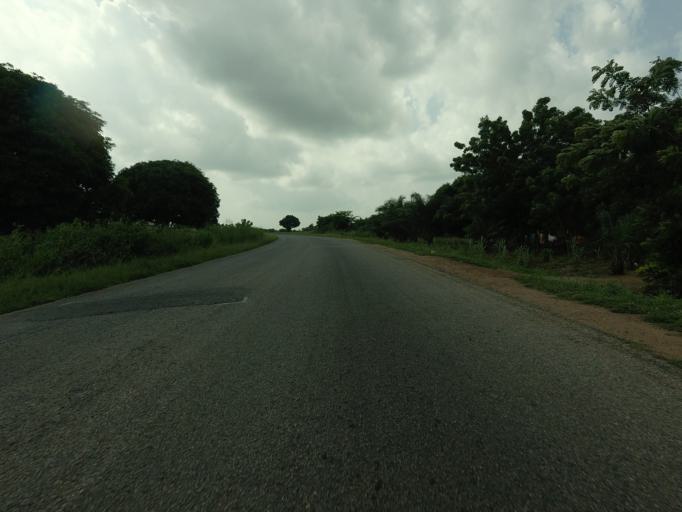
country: GH
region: Volta
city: Ho
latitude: 6.4321
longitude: 0.7322
